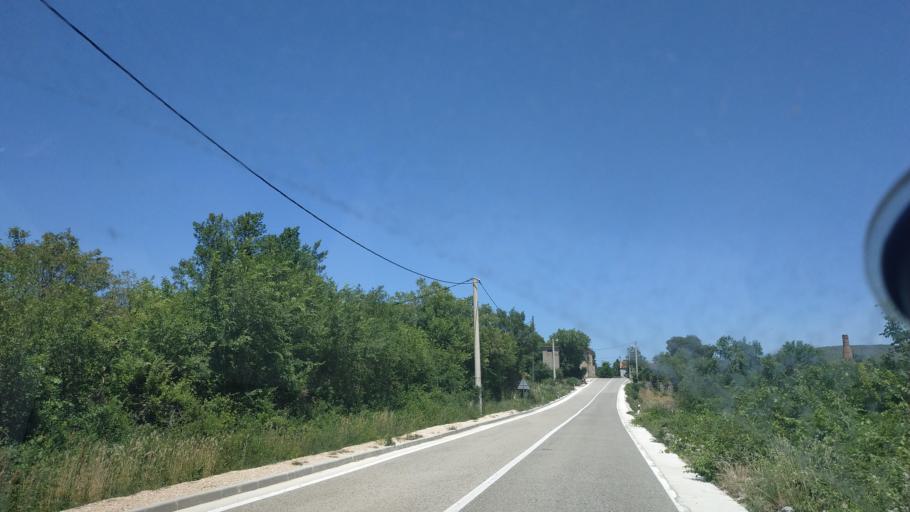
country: HR
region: Sibensko-Kniniska
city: Drnis
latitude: 43.8915
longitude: 16.2088
